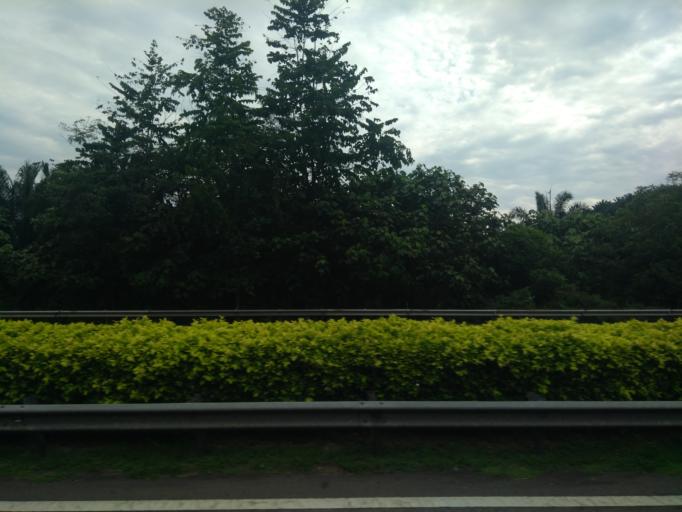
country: MY
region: Negeri Sembilan
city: Tampin
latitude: 2.4578
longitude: 102.1636
